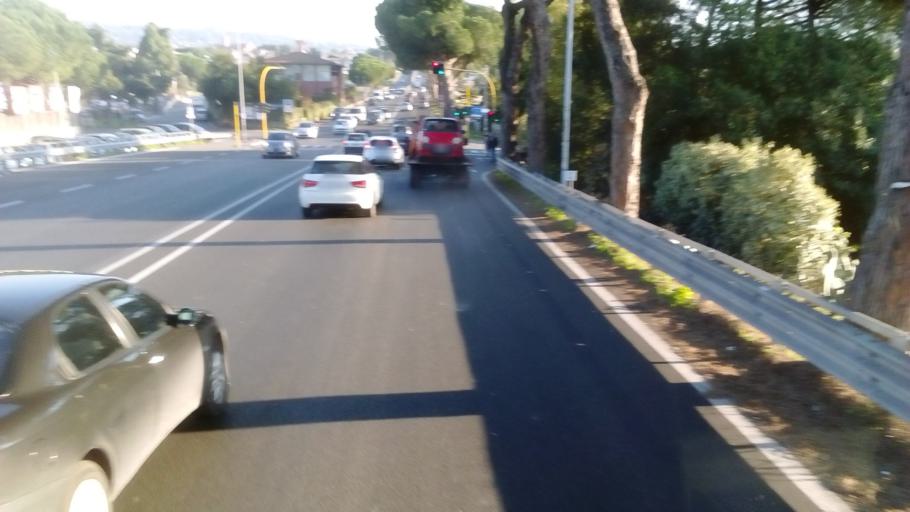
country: IT
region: Latium
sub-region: Citta metropolitana di Roma Capitale
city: Ciampino
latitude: 41.7759
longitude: 12.6076
